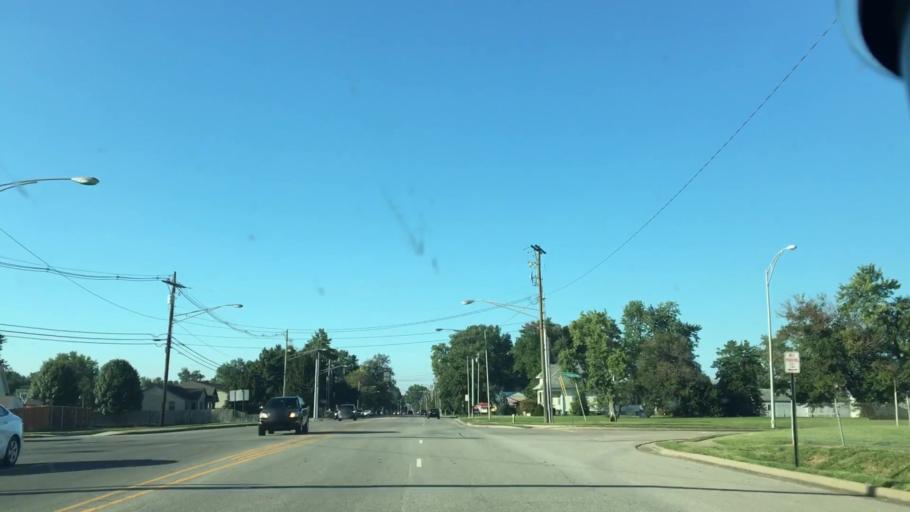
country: US
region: Indiana
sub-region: Vanderburgh County
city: Evansville
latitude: 37.9412
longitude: -87.4929
